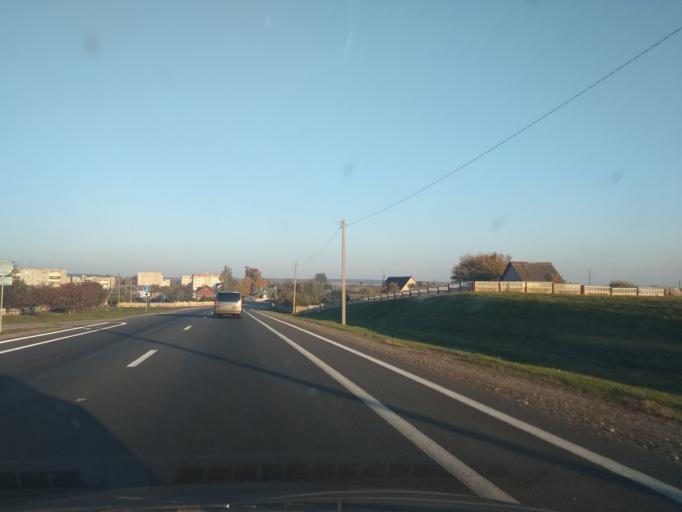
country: BY
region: Grodnenskaya
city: Zel'va
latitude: 53.1431
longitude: 24.8086
